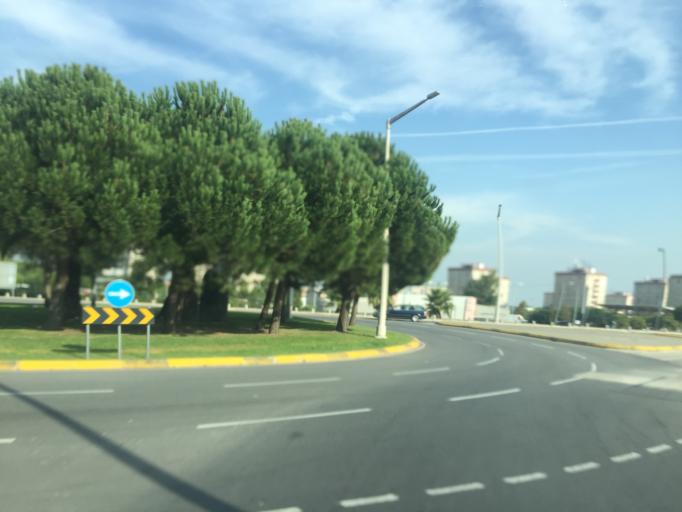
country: PT
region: Lisbon
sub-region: Loures
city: Sacavem
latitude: 38.7800
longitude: -9.1255
